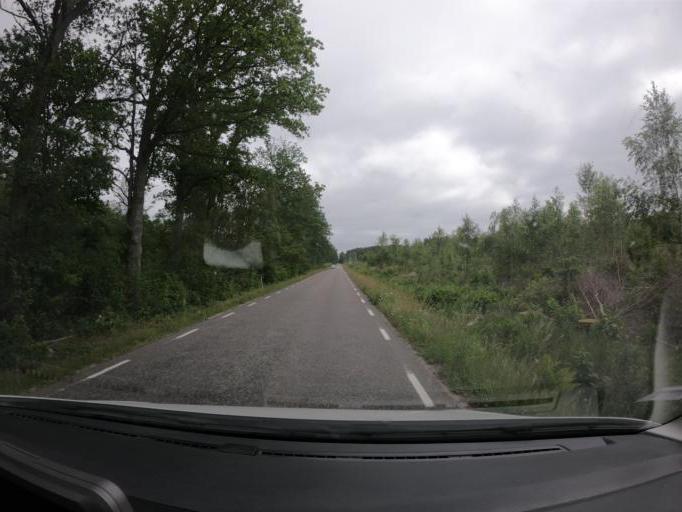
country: SE
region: Skane
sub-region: Hoors Kommun
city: Hoeoer
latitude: 55.9815
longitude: 13.4541
